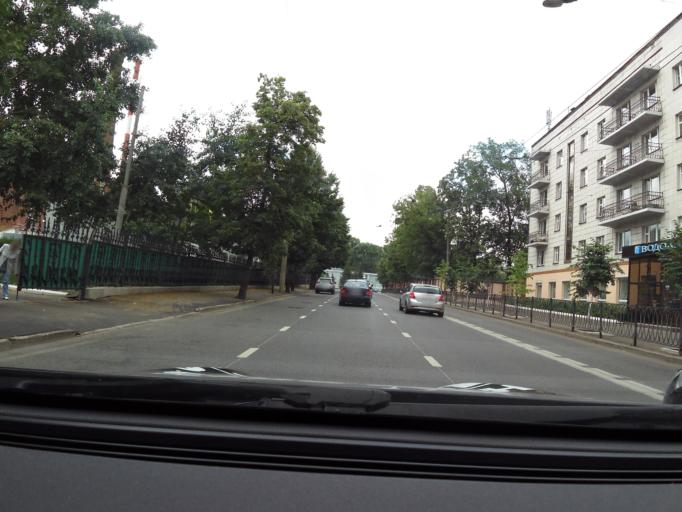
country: RU
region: Tatarstan
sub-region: Gorod Kazan'
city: Kazan
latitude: 55.7933
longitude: 49.1395
